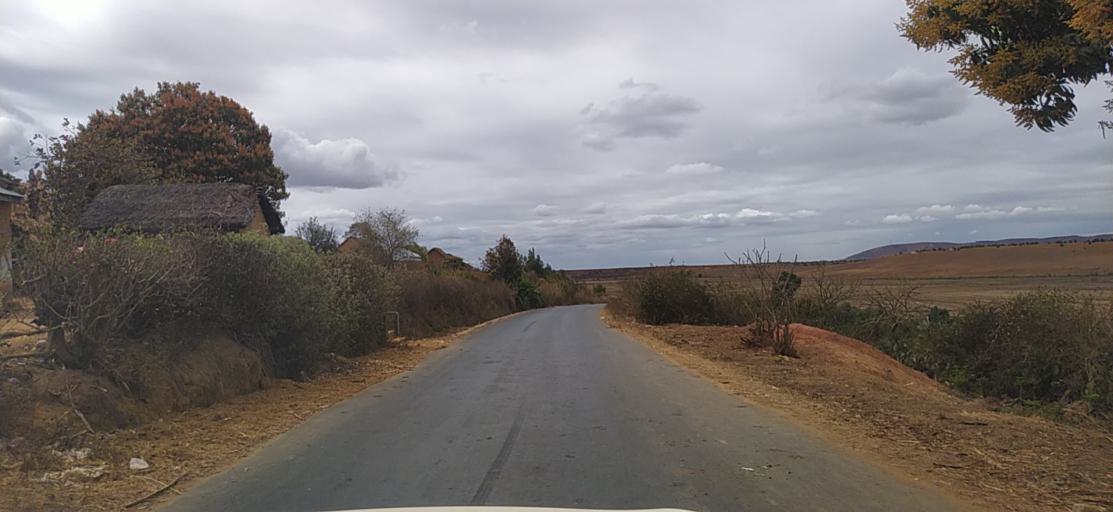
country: MG
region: Alaotra Mangoro
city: Ambatondrazaka
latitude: -17.9280
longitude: 48.2574
